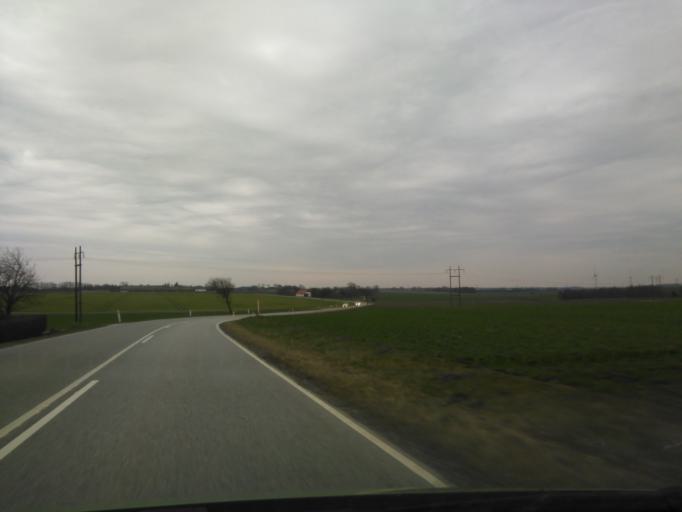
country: DK
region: North Denmark
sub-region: Mariagerfjord Kommune
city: Mariager
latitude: 56.5877
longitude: 9.9961
